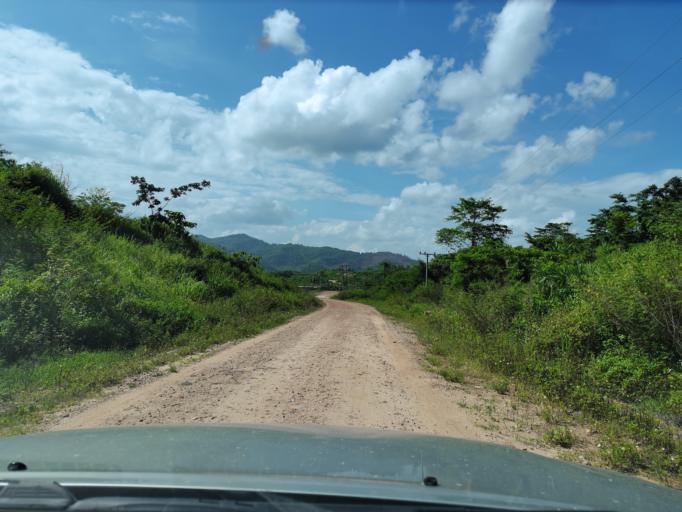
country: LA
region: Loungnamtha
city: Muang Nale
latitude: 20.5841
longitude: 101.0595
